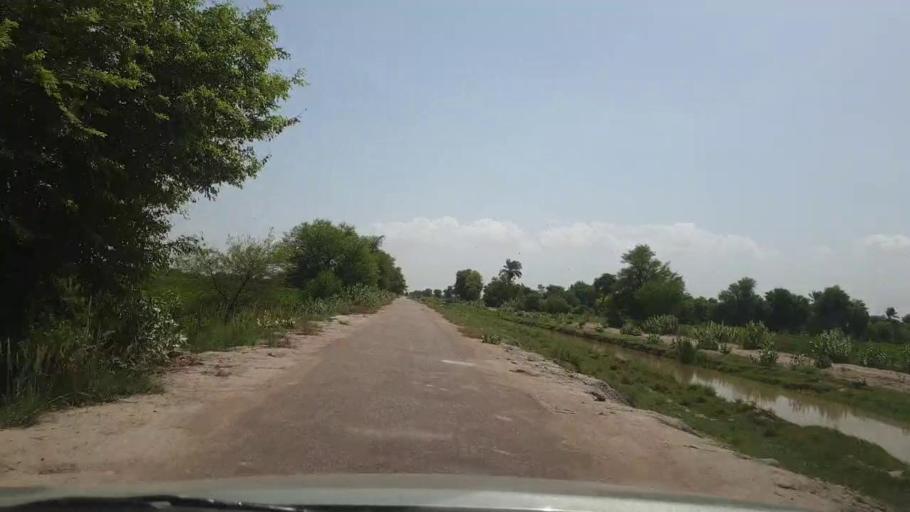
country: PK
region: Sindh
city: Pano Aqil
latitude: 27.7273
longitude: 69.0906
